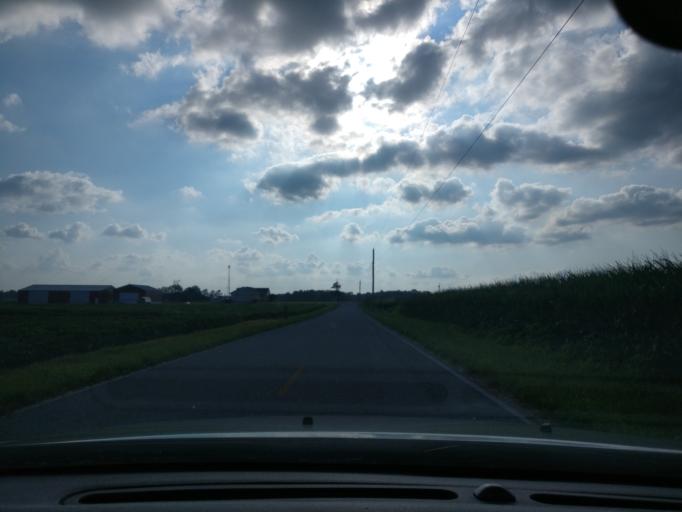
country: US
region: Ohio
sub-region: Clinton County
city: Wilmington
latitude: 39.5369
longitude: -83.8291
